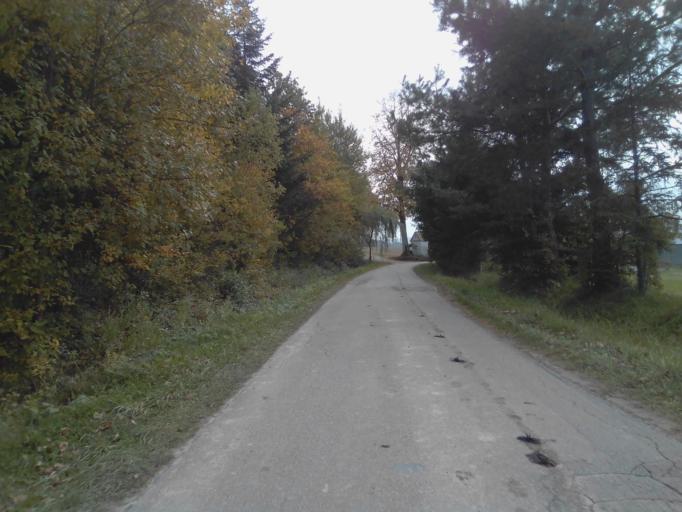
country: PL
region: Subcarpathian Voivodeship
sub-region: Powiat strzyzowski
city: Gwoznica Gorna
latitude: 49.8605
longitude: 21.9750
